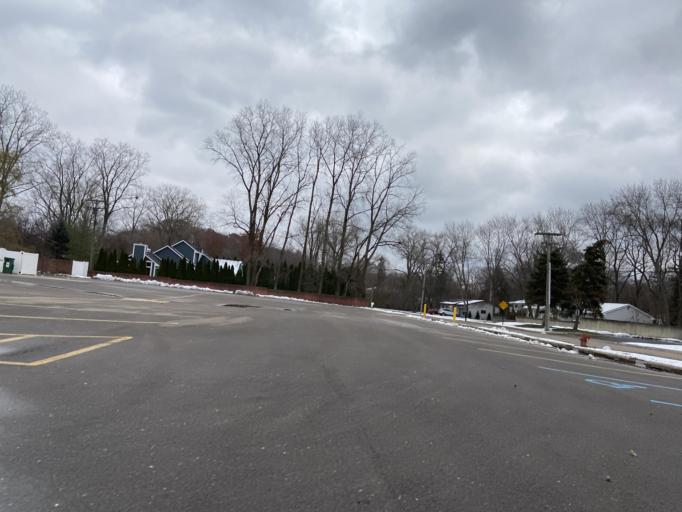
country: US
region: Michigan
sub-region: Oakland County
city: Farmington
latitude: 42.4639
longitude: -83.3561
